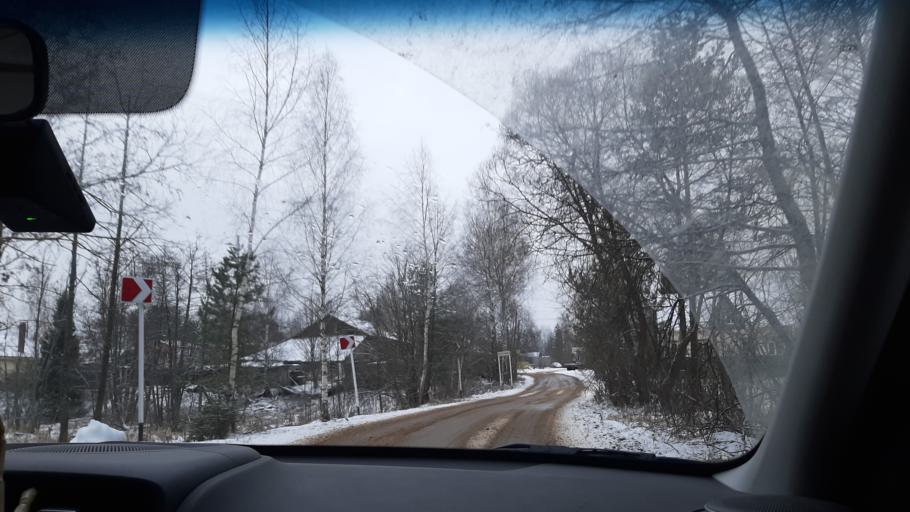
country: RU
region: Ivanovo
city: Kokhma
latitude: 56.9022
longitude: 41.0084
